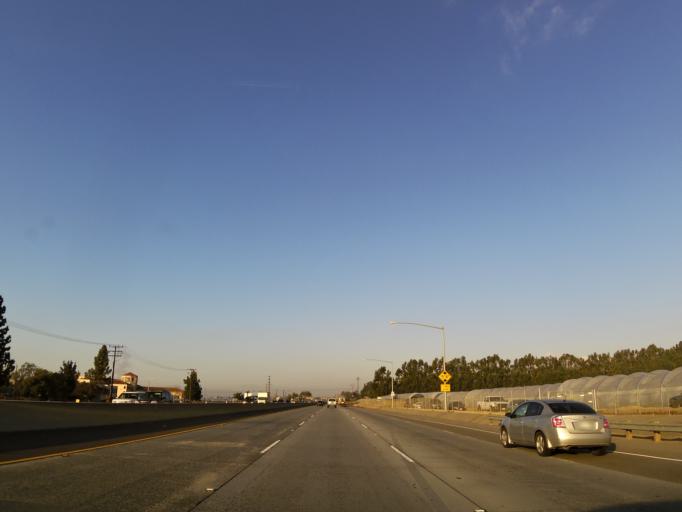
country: US
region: California
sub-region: Ventura County
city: Camarillo
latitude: 34.2211
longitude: -119.0926
